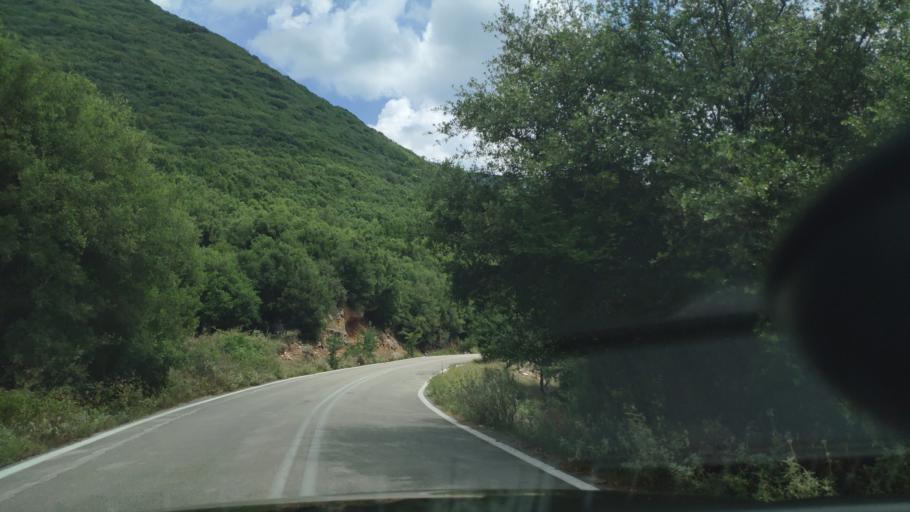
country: GR
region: Epirus
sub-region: Nomos Artas
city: Kampi
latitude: 39.2747
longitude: 20.9526
